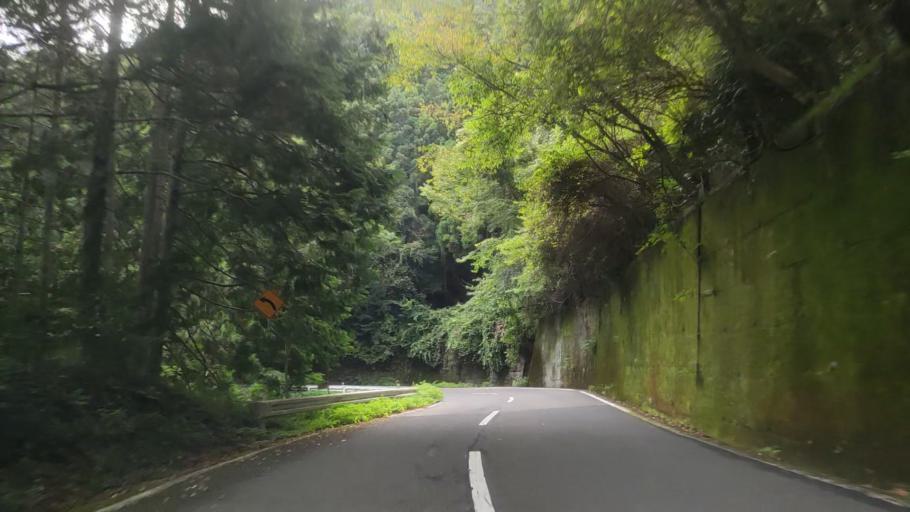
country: JP
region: Wakayama
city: Koya
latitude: 34.2529
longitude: 135.5444
